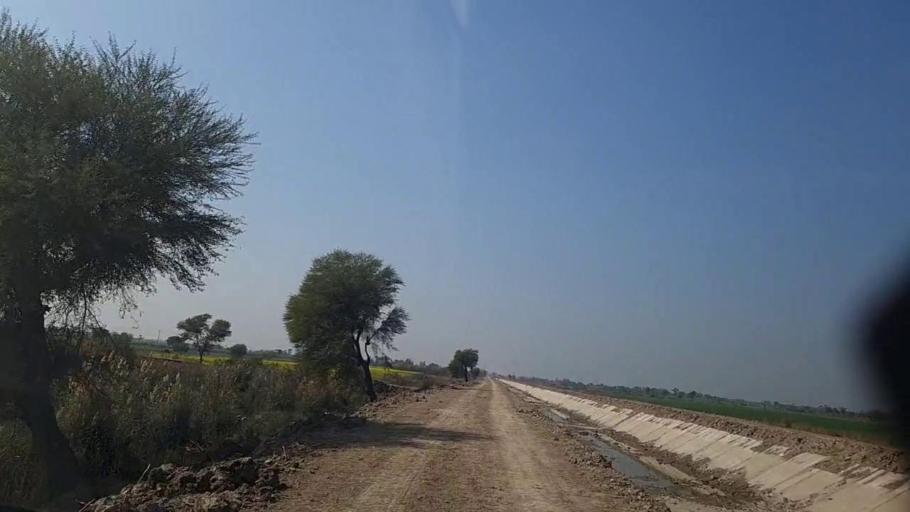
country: PK
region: Sindh
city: Sakrand
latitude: 26.1470
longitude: 68.3540
